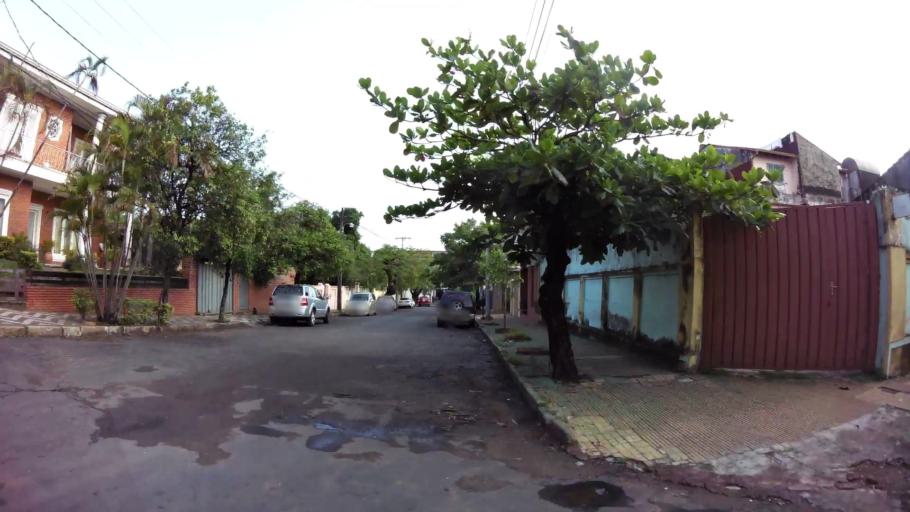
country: PY
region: Presidente Hayes
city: Nanawa
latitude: -25.2780
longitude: -57.6493
